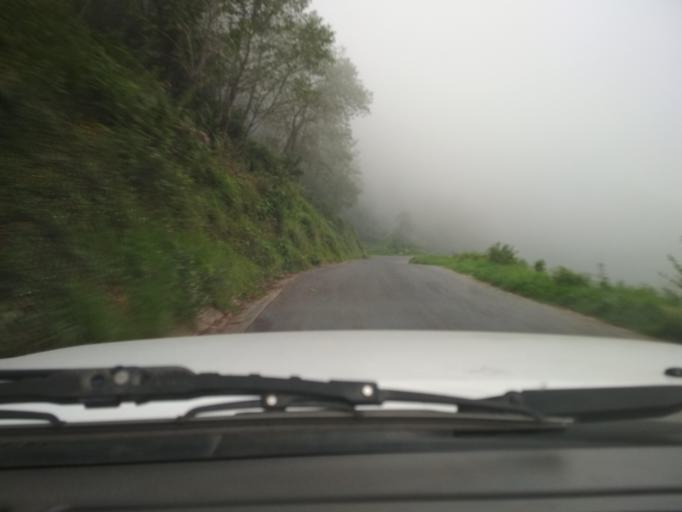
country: MX
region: Veracruz
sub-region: La Perla
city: Metlac Hernandez (Metlac Primero)
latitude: 18.9684
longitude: -97.1464
